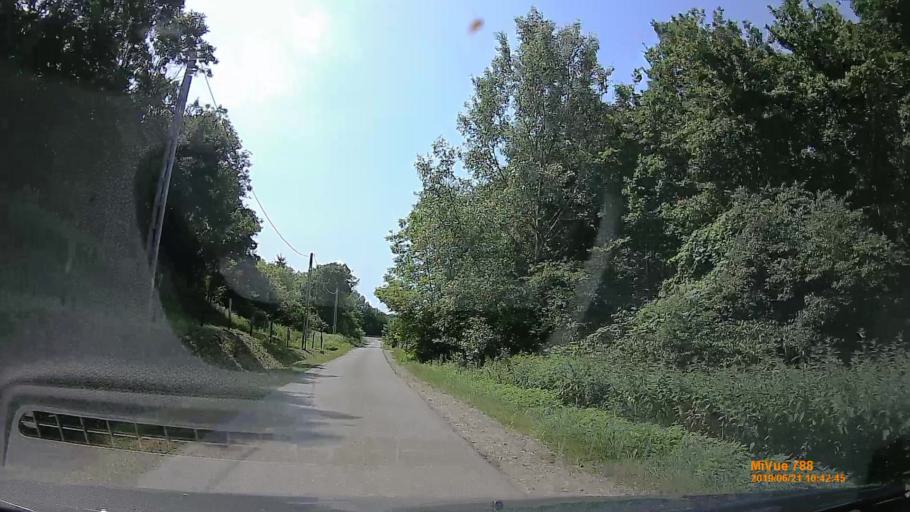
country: HU
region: Baranya
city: Buekkoesd
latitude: 46.1276
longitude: 18.0050
